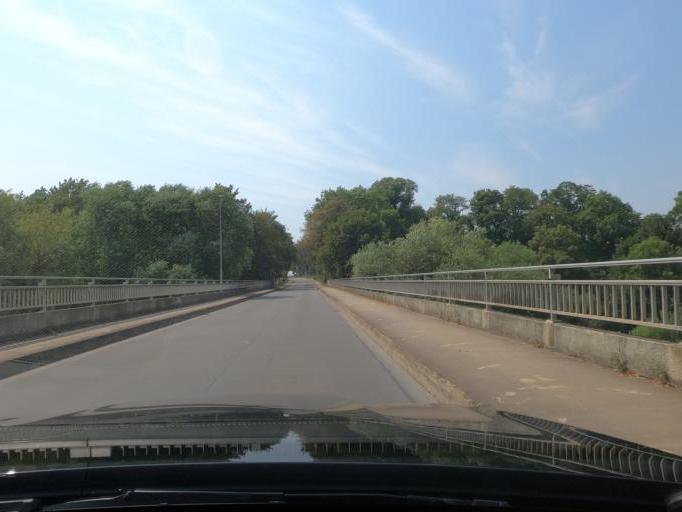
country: DE
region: Lower Saxony
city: Sarstedt
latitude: 52.2459
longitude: 9.8278
